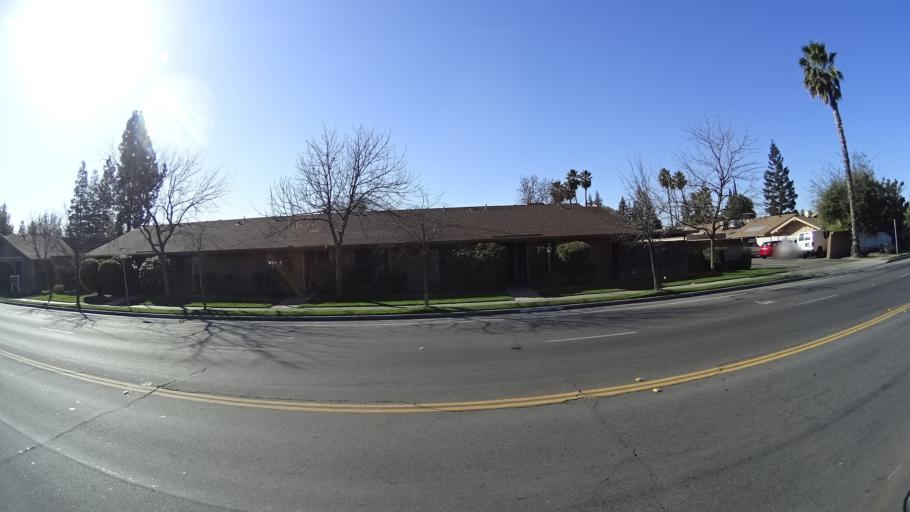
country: US
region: California
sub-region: Fresno County
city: Fresno
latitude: 36.8229
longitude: -119.8067
